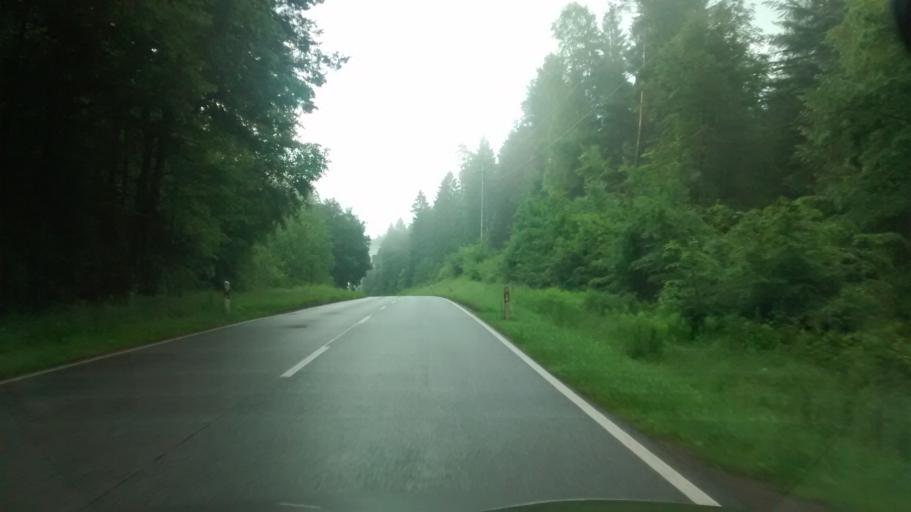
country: DE
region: Rheinland-Pfalz
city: Vorderweidenthal
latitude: 49.1147
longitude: 7.8828
